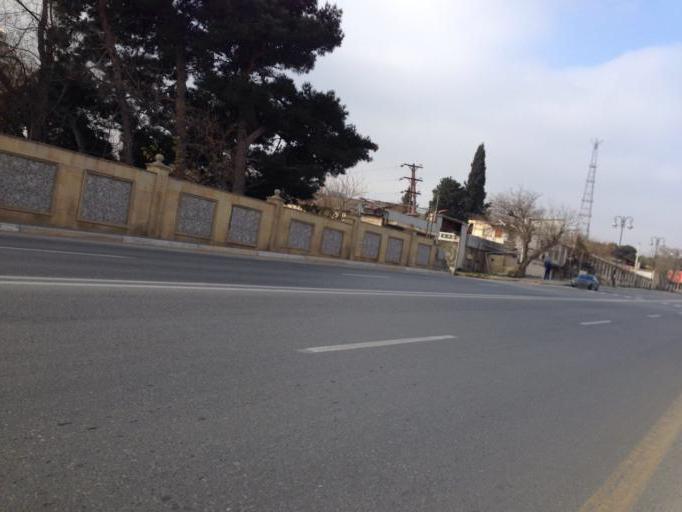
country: AZ
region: Baki
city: Baku
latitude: 40.3938
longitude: 49.8548
